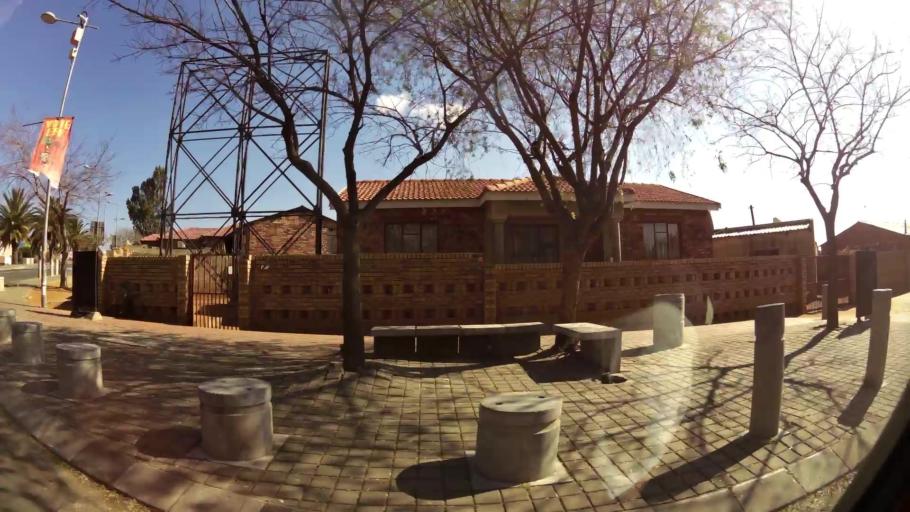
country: ZA
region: Gauteng
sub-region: City of Johannesburg Metropolitan Municipality
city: Soweto
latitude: -26.2377
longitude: 27.9064
